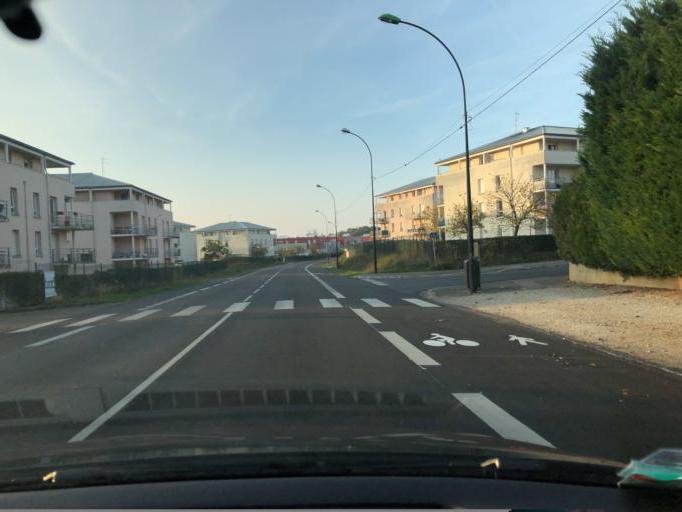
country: FR
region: Bourgogne
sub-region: Departement de l'Yonne
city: Saint-Clement
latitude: 48.2043
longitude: 3.2956
